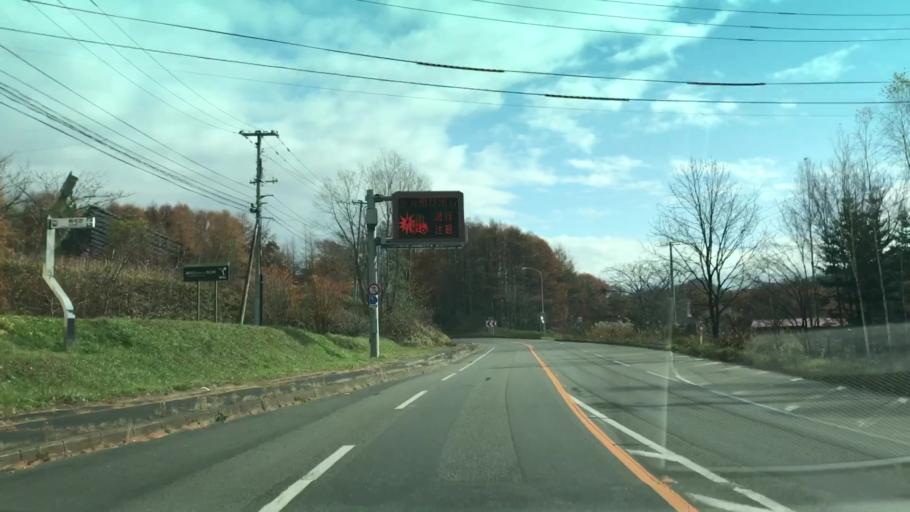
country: JP
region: Hokkaido
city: Shizunai-furukawacho
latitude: 42.7178
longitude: 142.2622
